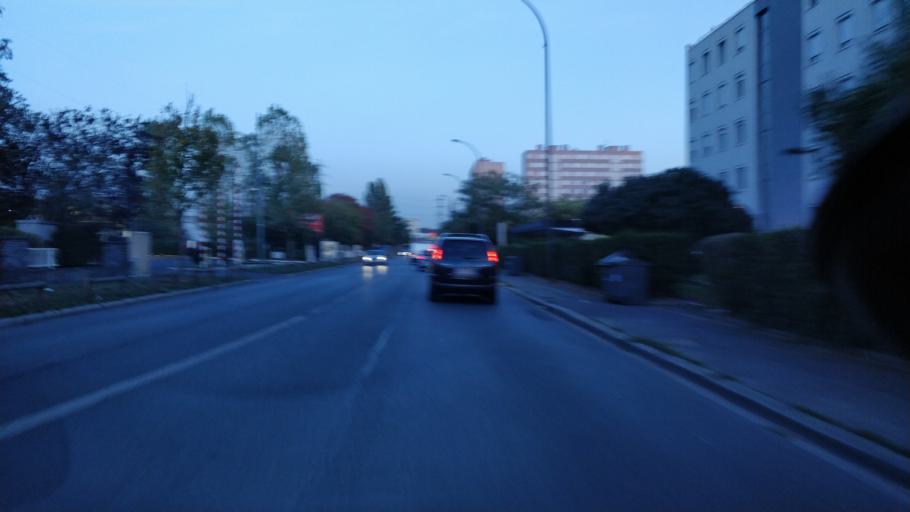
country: FR
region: Ile-de-France
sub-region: Departement de Seine-Saint-Denis
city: Villemomble
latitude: 48.8847
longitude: 2.4829
